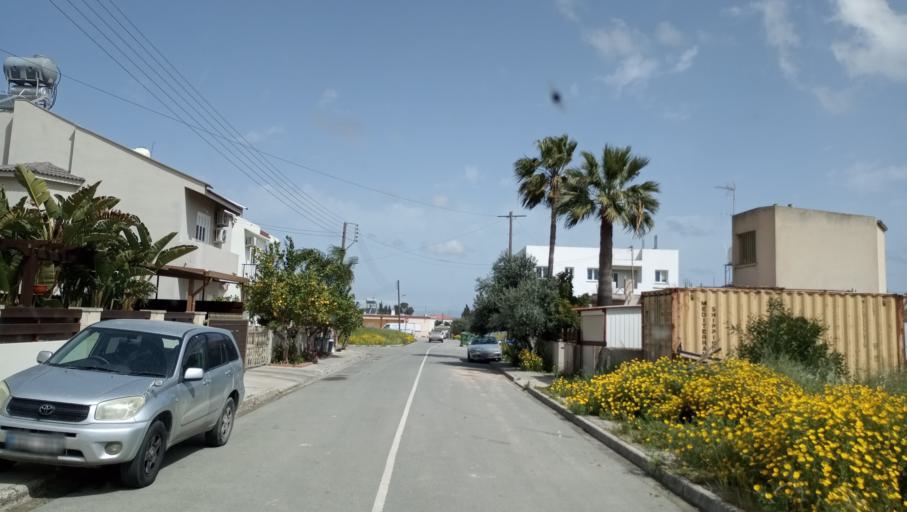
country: CY
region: Lefkosia
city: Dali
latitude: 35.0236
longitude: 33.4326
